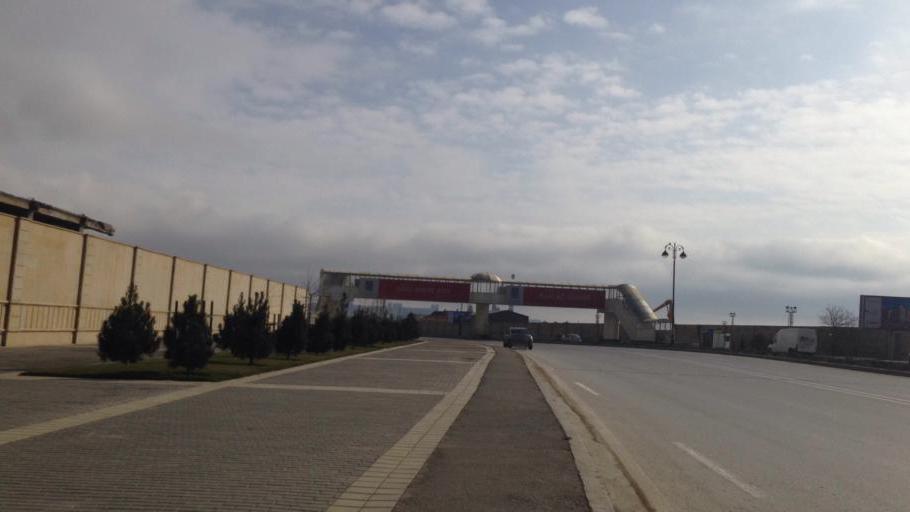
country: AZ
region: Baki
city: Baku
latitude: 40.3785
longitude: 49.8902
